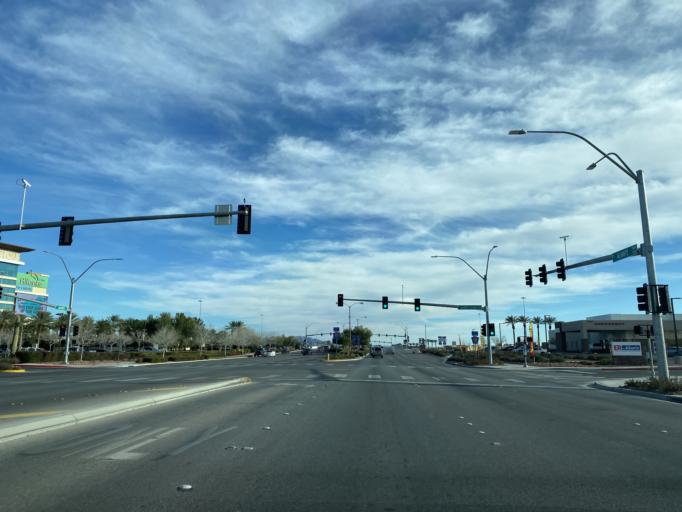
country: US
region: Nevada
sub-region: Clark County
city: North Las Vegas
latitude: 36.2919
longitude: -115.1830
